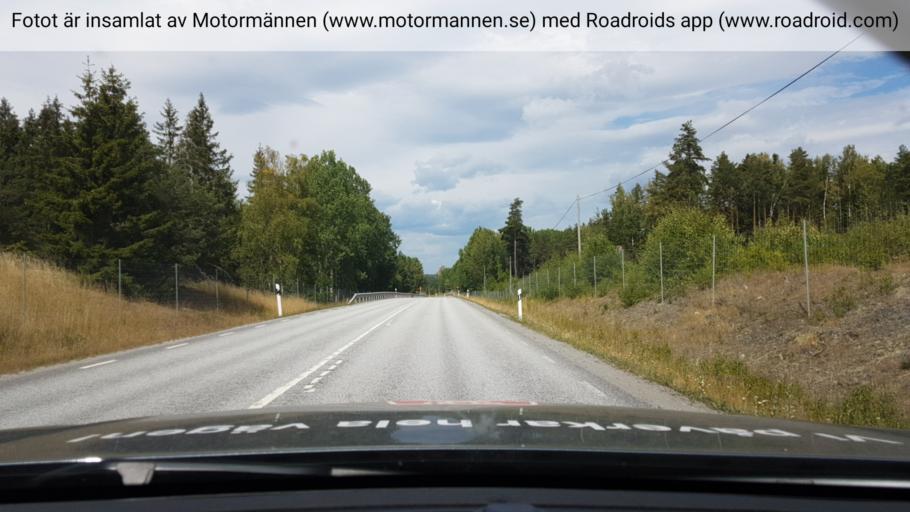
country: SE
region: Uppsala
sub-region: Habo Kommun
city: Balsta
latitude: 59.6071
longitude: 17.6081
